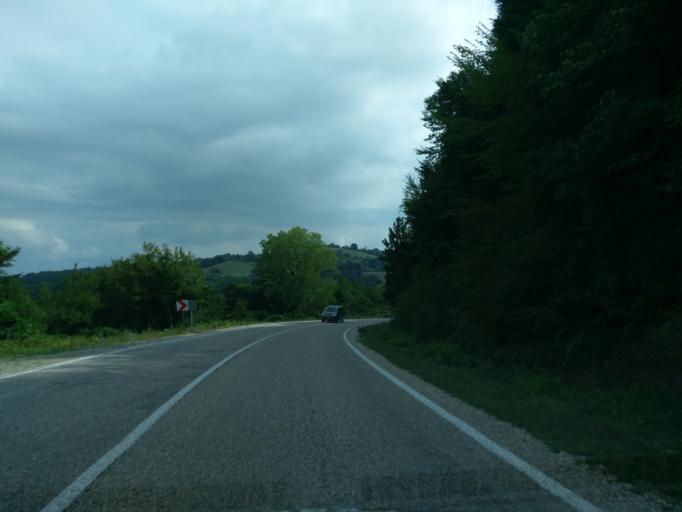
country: TR
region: Sinop
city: Erfelek
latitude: 41.9592
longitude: 34.8270
